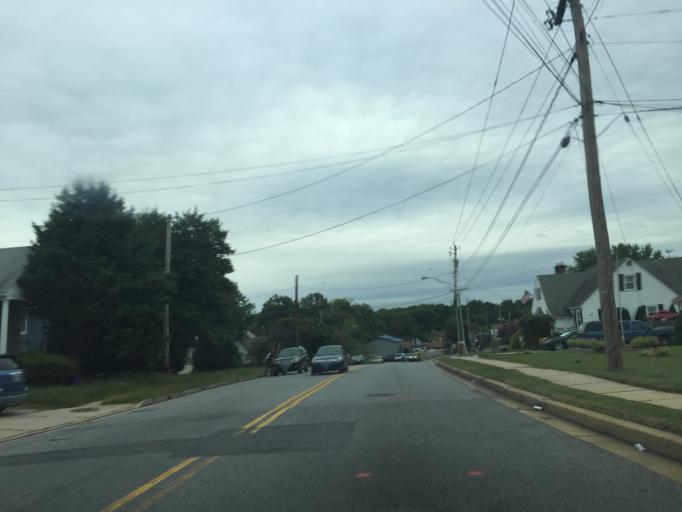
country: US
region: Maryland
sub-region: Baltimore County
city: Overlea
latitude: 39.3421
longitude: -76.5300
